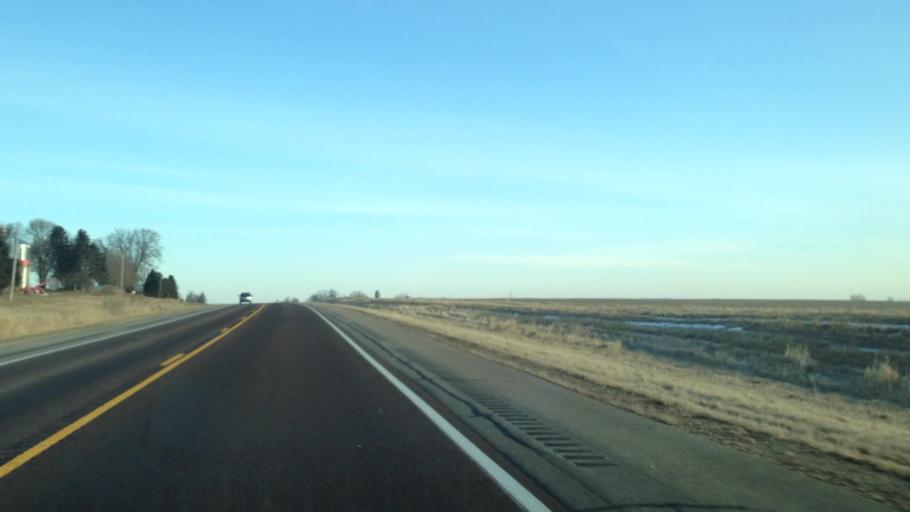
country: US
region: Minnesota
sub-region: Goodhue County
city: Zumbrota
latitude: 44.3294
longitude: -92.6453
